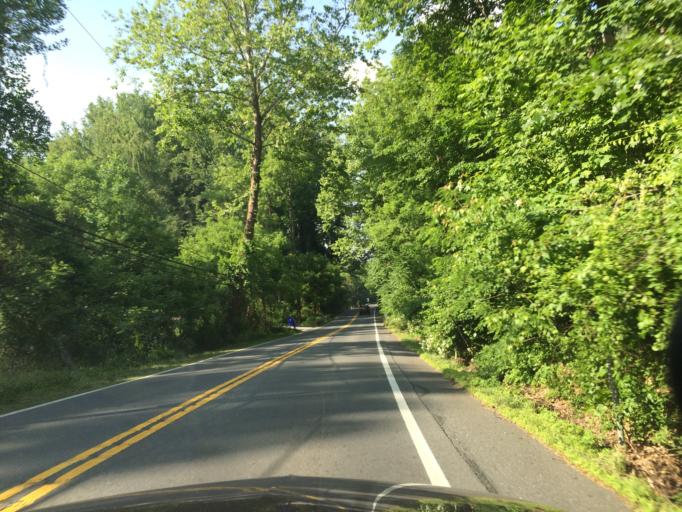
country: US
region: Maryland
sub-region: Montgomery County
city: Olney
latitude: 39.1974
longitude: -77.0668
